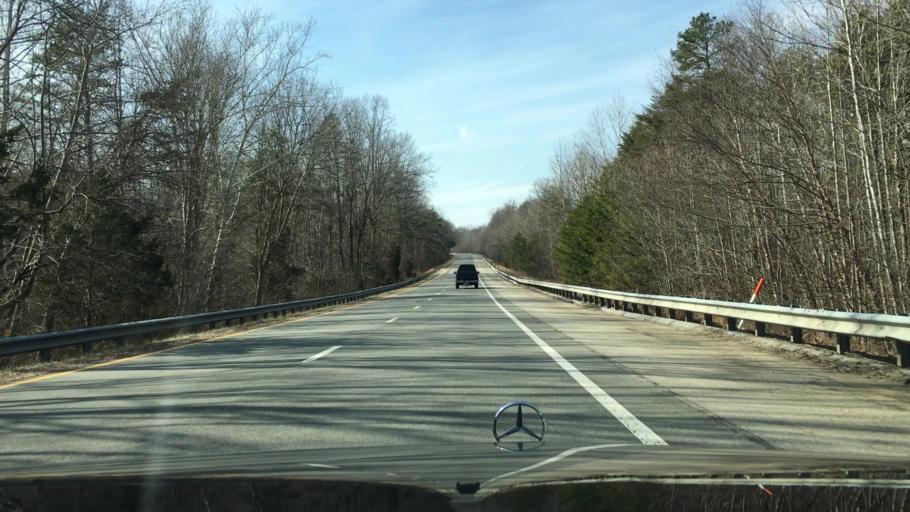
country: US
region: Virginia
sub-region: Prince Edward County
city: Hampden Sydney
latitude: 37.3146
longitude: -78.4832
